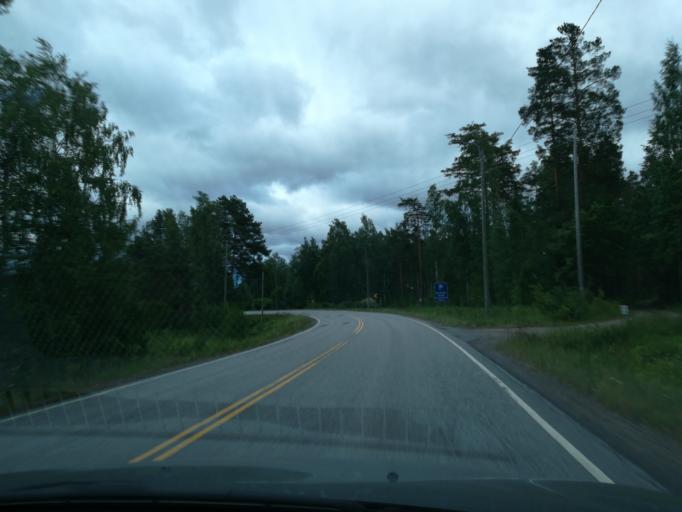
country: FI
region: Southern Savonia
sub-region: Mikkeli
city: Ristiina
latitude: 61.3509
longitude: 27.3917
